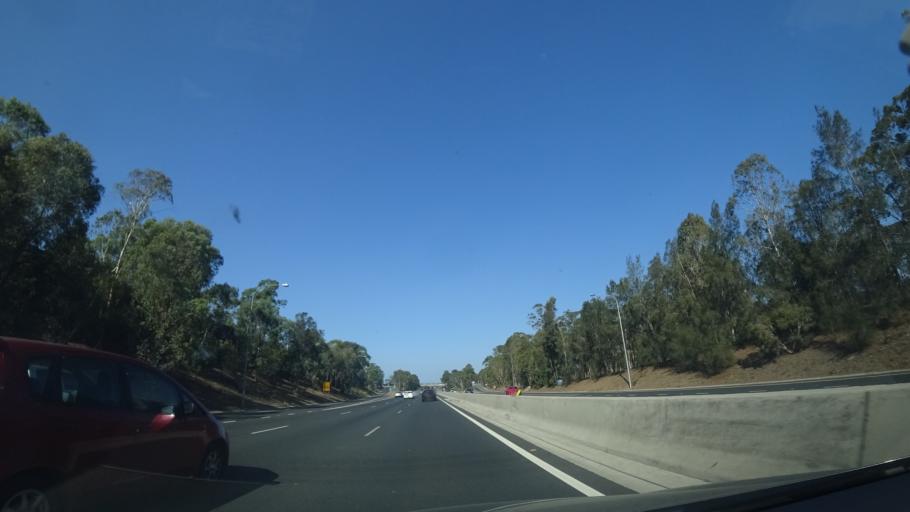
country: AU
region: New South Wales
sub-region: Bankstown
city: Milperra
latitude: -33.9452
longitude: 150.9778
